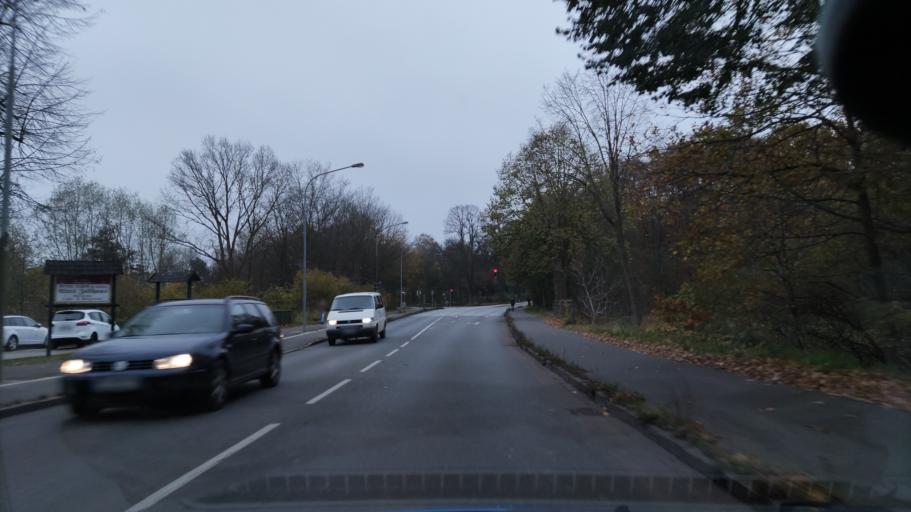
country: DE
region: Schleswig-Holstein
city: Luebeck
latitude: 53.8339
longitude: 10.7154
